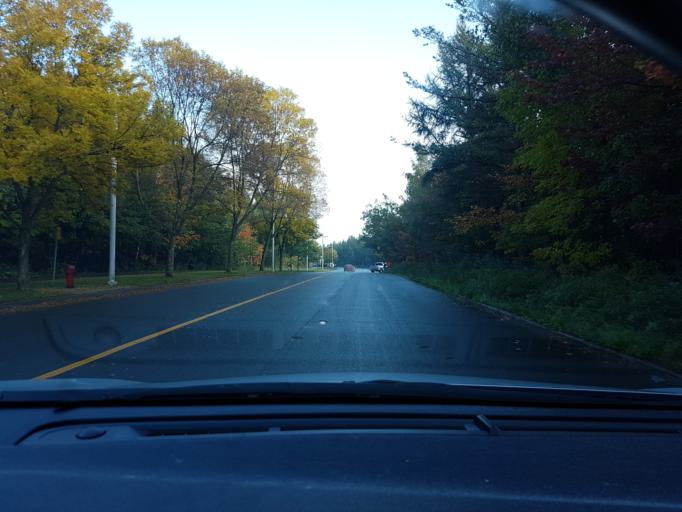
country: CA
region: Quebec
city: L'Ancienne-Lorette
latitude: 46.8004
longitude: -71.3183
